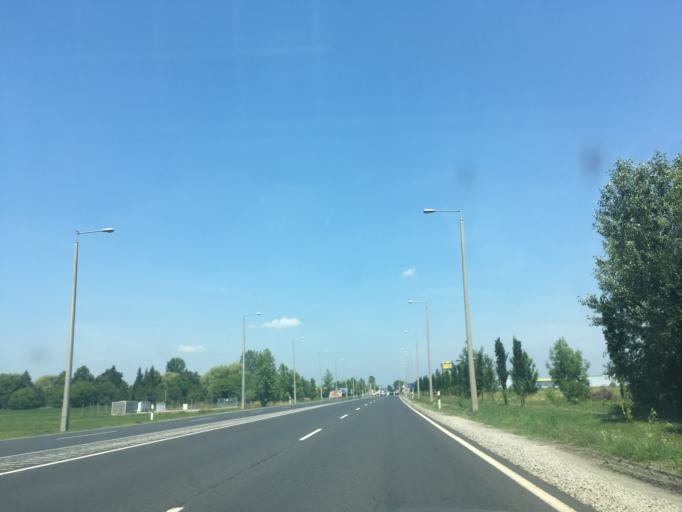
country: HU
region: Hajdu-Bihar
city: Mikepercs
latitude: 47.4907
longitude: 21.6326
